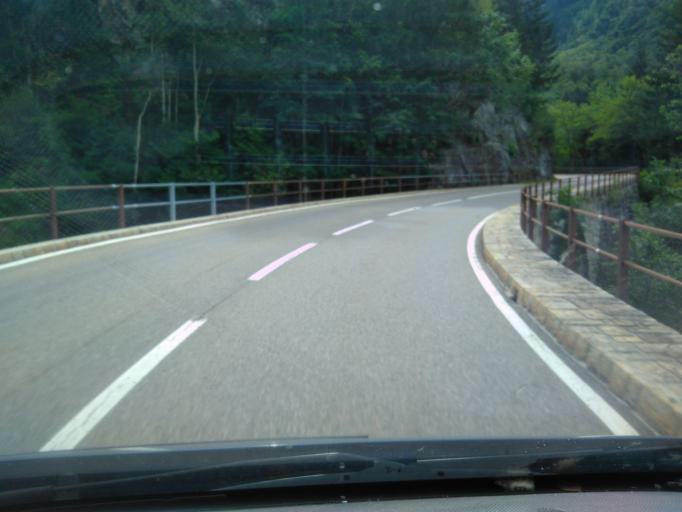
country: CH
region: Bern
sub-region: Interlaken-Oberhasli District
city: Meiringen
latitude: 46.7206
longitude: 8.2979
